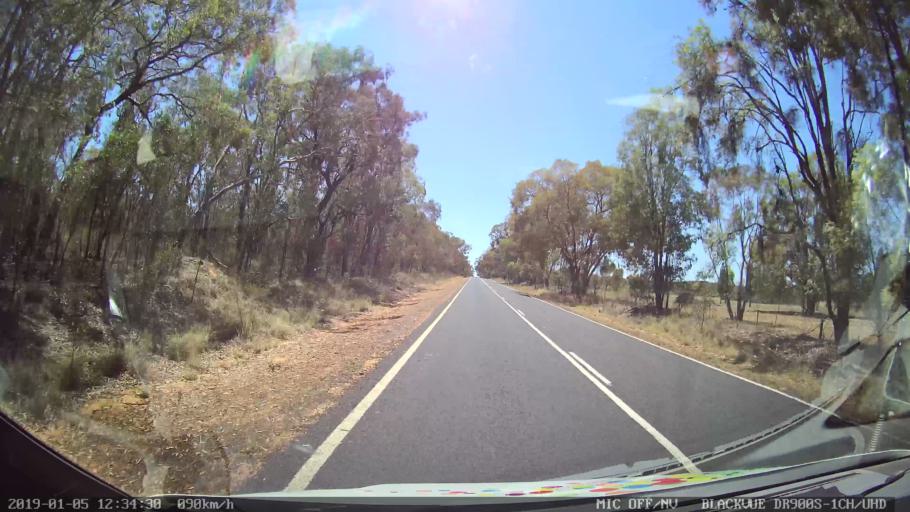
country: AU
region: New South Wales
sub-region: Warrumbungle Shire
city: Coonabarabran
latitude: -31.2119
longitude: 149.4114
